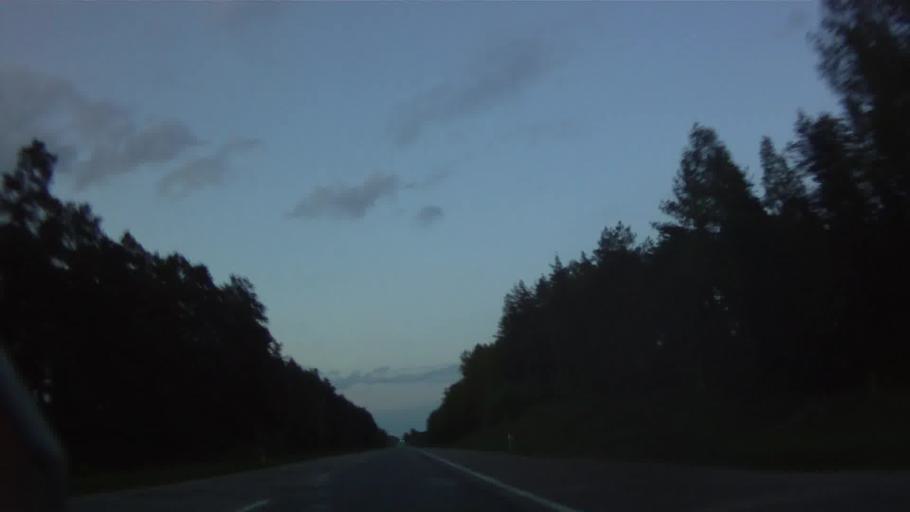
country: LV
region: Incukalns
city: Vangazi
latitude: 57.0829
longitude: 24.5326
